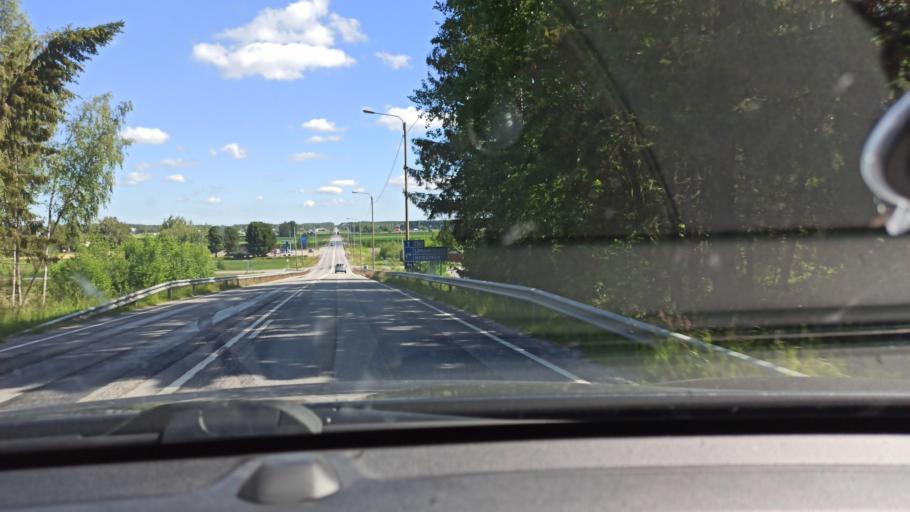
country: FI
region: Ostrobothnia
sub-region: Vaasa
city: Teeriniemi
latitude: 62.9993
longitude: 21.6675
